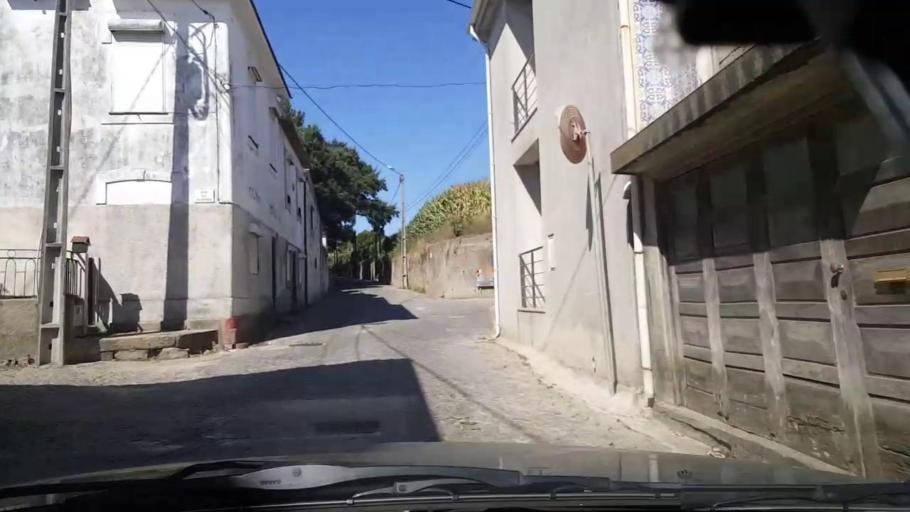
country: PT
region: Porto
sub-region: Vila do Conde
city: Arvore
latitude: 41.3152
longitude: -8.6731
